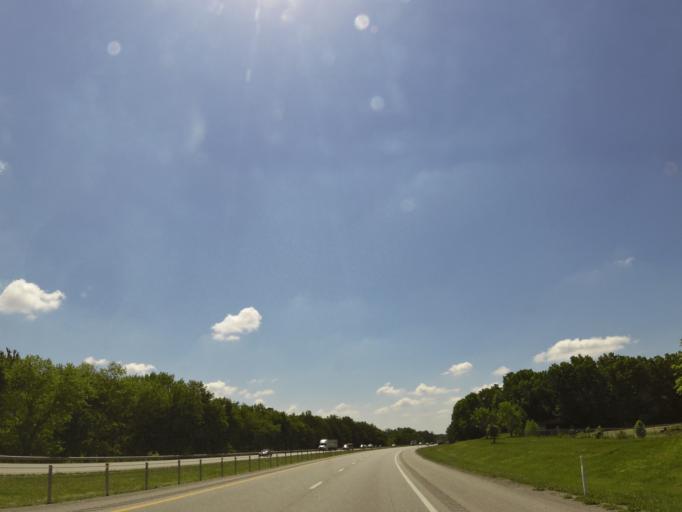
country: US
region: Kentucky
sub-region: Laurel County
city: London
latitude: 37.2034
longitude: -84.1601
